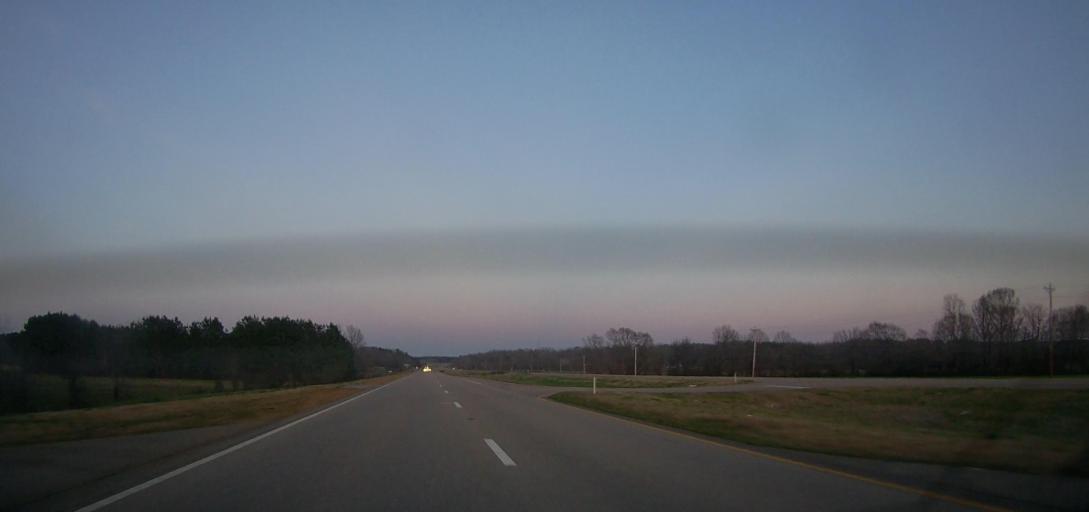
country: US
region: Mississippi
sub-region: Tippah County
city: Ripley
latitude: 34.9536
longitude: -88.8751
